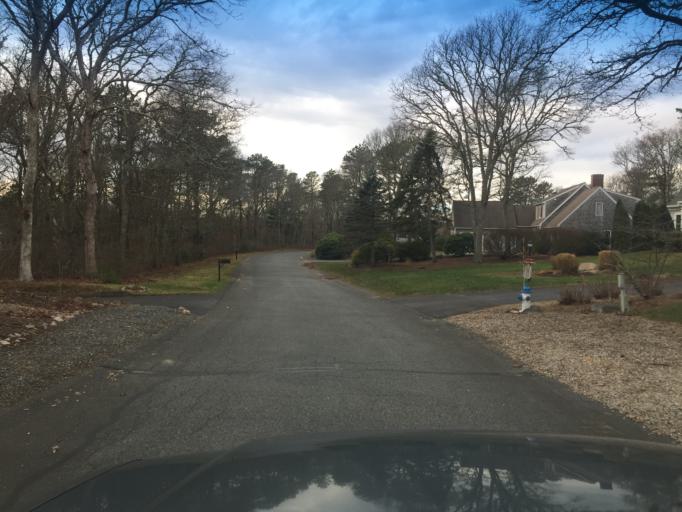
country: US
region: Massachusetts
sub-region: Barnstable County
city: North Falmouth
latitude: 41.6371
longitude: -70.6145
